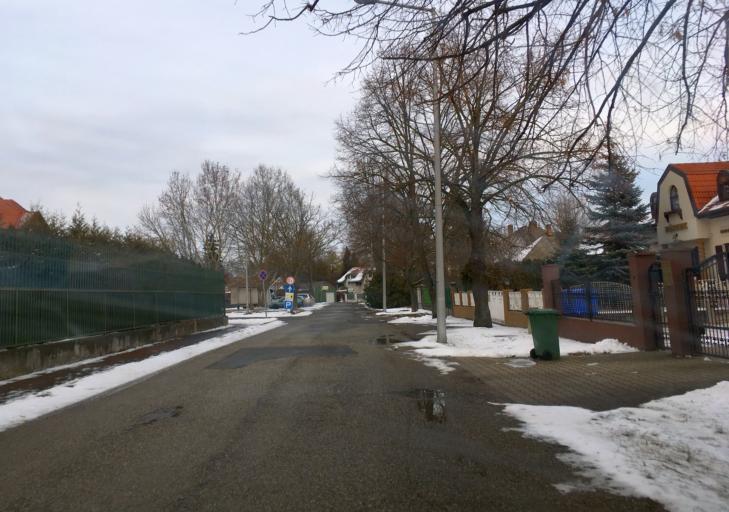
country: HU
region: Gyor-Moson-Sopron
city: Mosonmagyarovar
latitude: 47.8764
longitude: 17.2789
